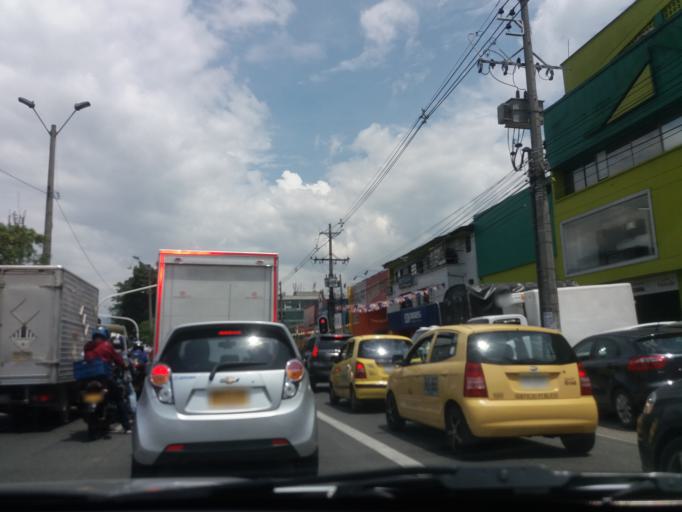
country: CO
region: Antioquia
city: Itagui
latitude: 6.2006
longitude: -75.5886
